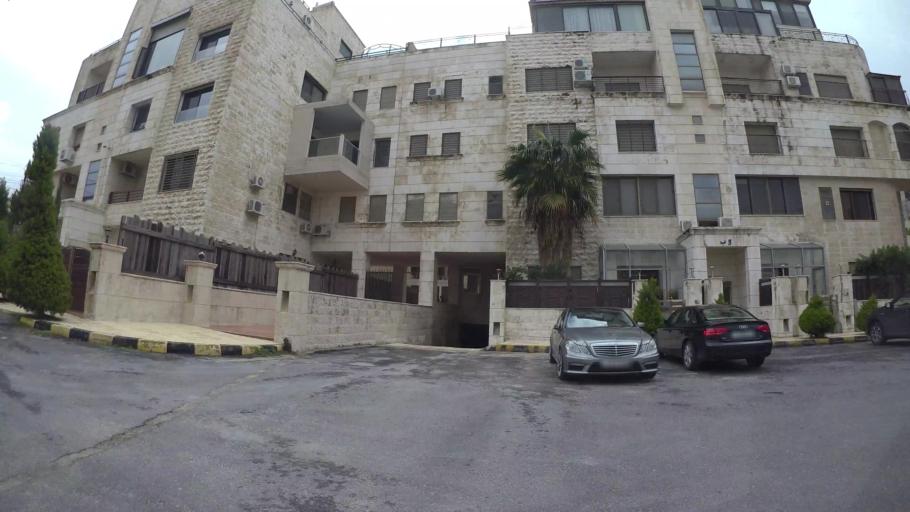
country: JO
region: Amman
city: Al Bunayyat ash Shamaliyah
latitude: 31.9410
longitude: 35.8939
